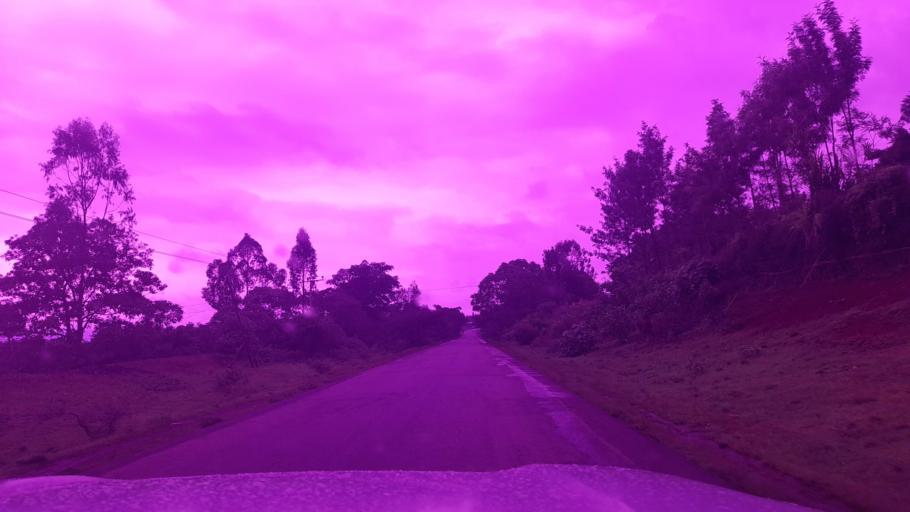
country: ET
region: Oromiya
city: Jima
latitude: 7.7028
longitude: 37.2519
